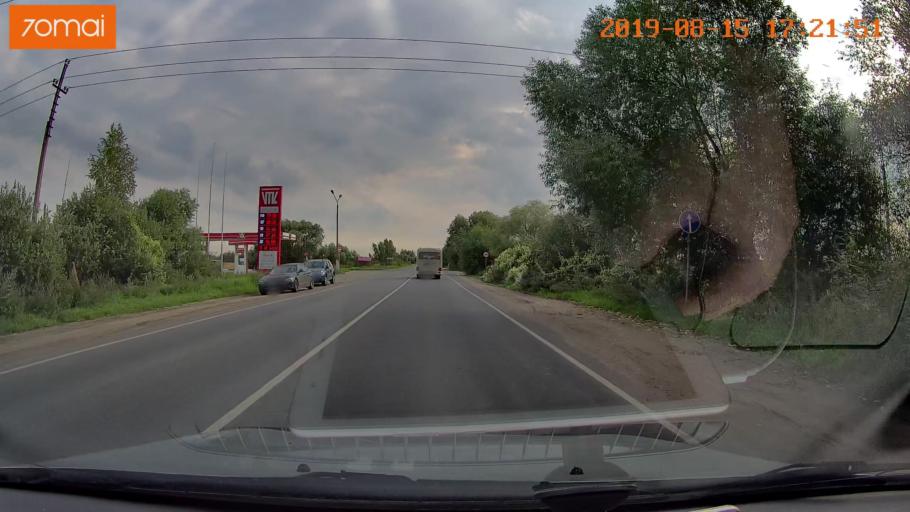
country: RU
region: Moskovskaya
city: Ashitkovo
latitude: 55.4194
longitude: 38.5667
